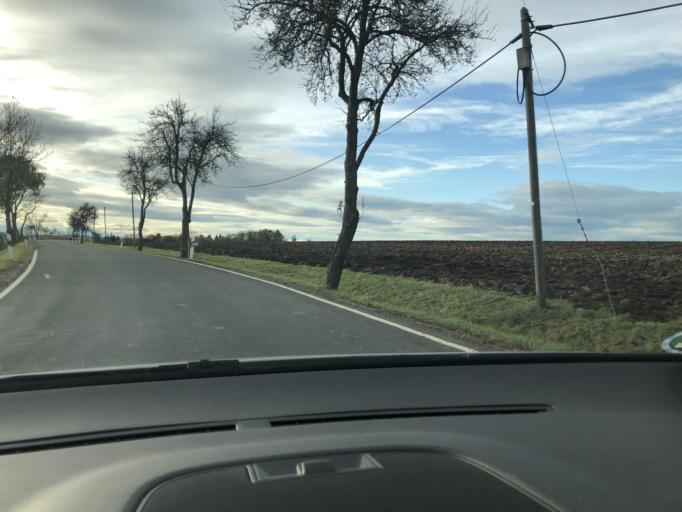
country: DE
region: Thuringia
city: Lehesten
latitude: 50.9608
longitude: 11.5632
